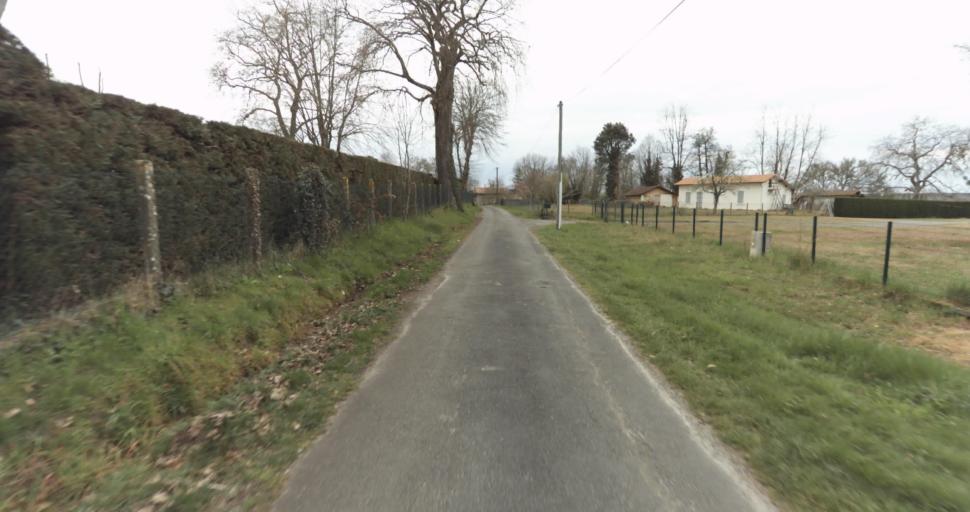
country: FR
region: Aquitaine
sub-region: Departement des Landes
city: Roquefort
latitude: 44.0290
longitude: -0.3240
